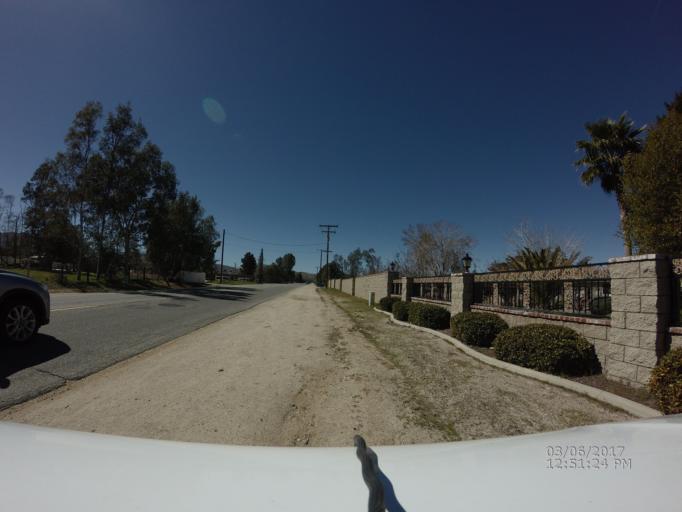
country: US
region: California
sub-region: Los Angeles County
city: Desert View Highlands
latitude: 34.6092
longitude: -118.1591
